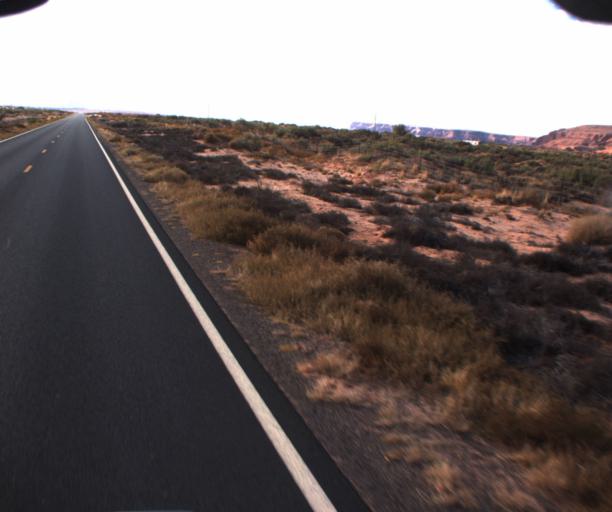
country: US
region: Arizona
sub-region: Apache County
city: Many Farms
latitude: 36.6568
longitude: -109.5943
